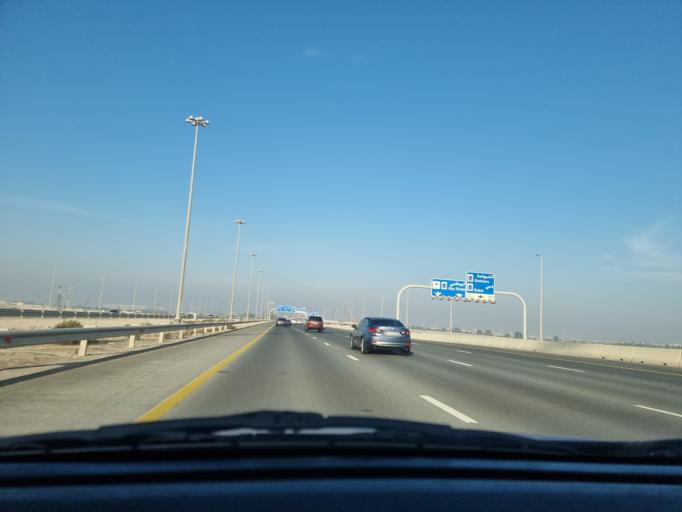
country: AE
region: Abu Dhabi
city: Abu Dhabi
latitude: 24.4820
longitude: 54.6564
